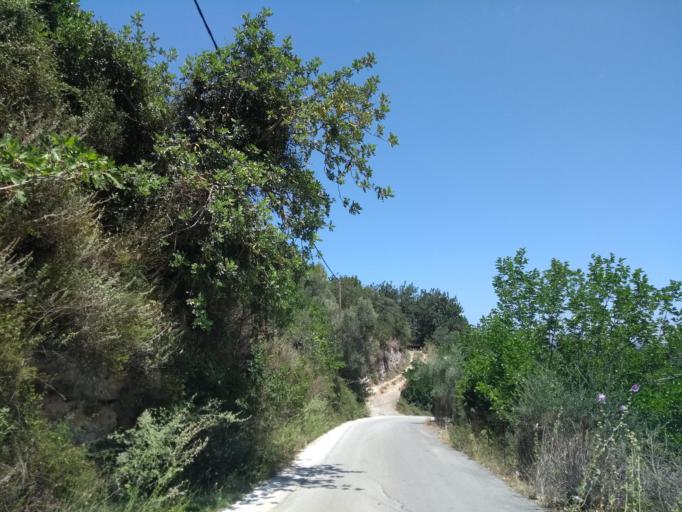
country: GR
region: Crete
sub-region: Nomos Chanias
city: Georgioupolis
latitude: 35.3170
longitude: 24.3029
